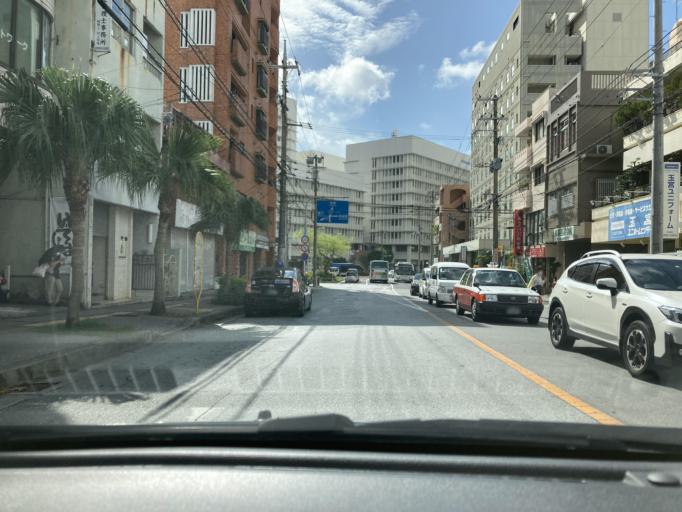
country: JP
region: Okinawa
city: Naha-shi
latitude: 26.2105
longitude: 127.6791
